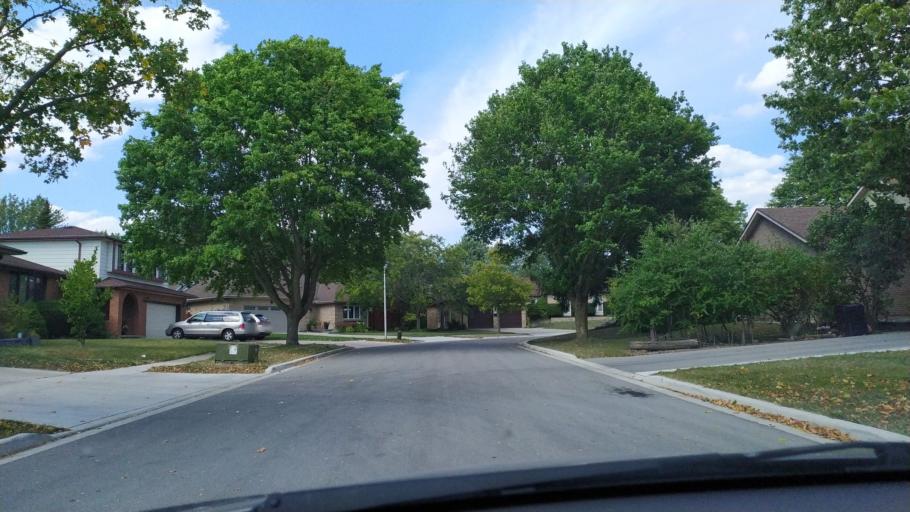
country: CA
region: Ontario
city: London
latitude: 42.9477
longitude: -81.2426
